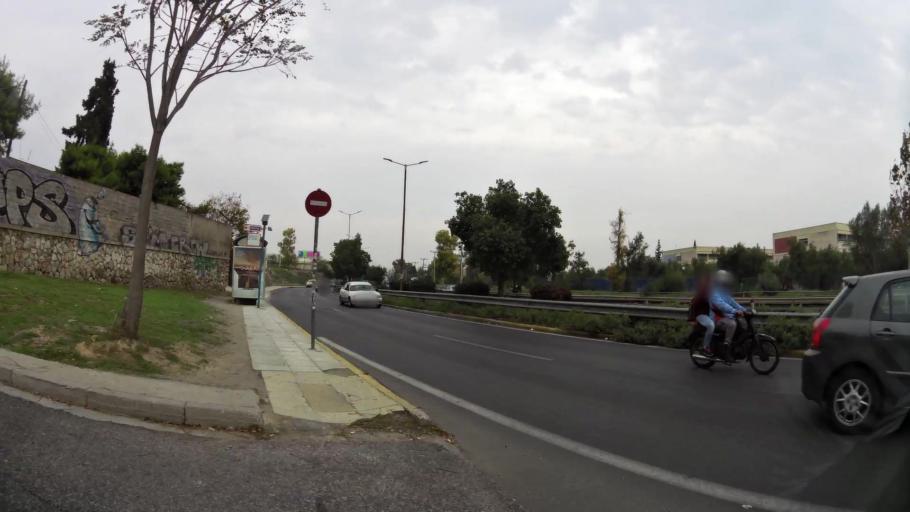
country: GR
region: Attica
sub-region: Nomos Piraios
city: Agios Ioannis Rentis
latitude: 37.9777
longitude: 23.6691
